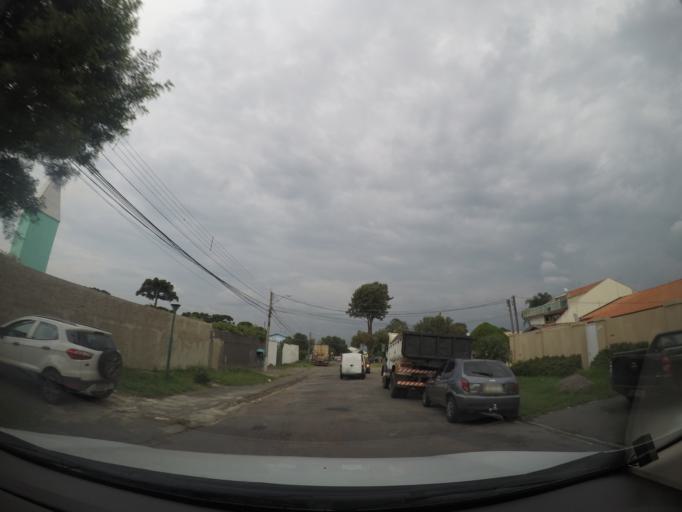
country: BR
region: Parana
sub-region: Sao Jose Dos Pinhais
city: Sao Jose dos Pinhais
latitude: -25.5232
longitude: -49.2363
